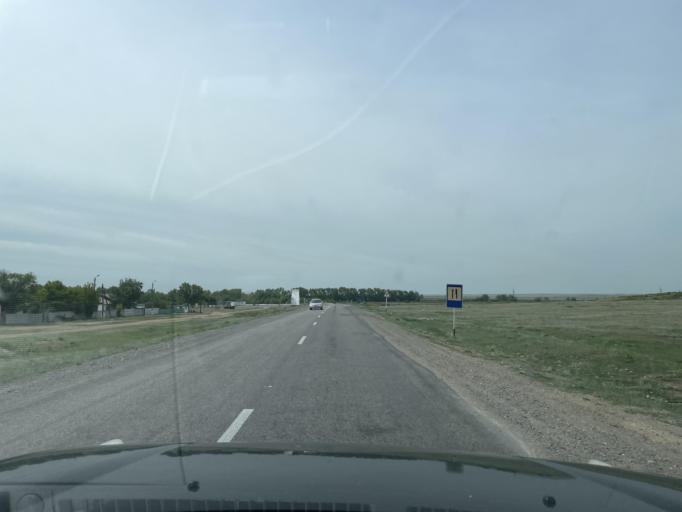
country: KZ
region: Qaraghandy
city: Abay
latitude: 49.4258
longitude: 72.9116
